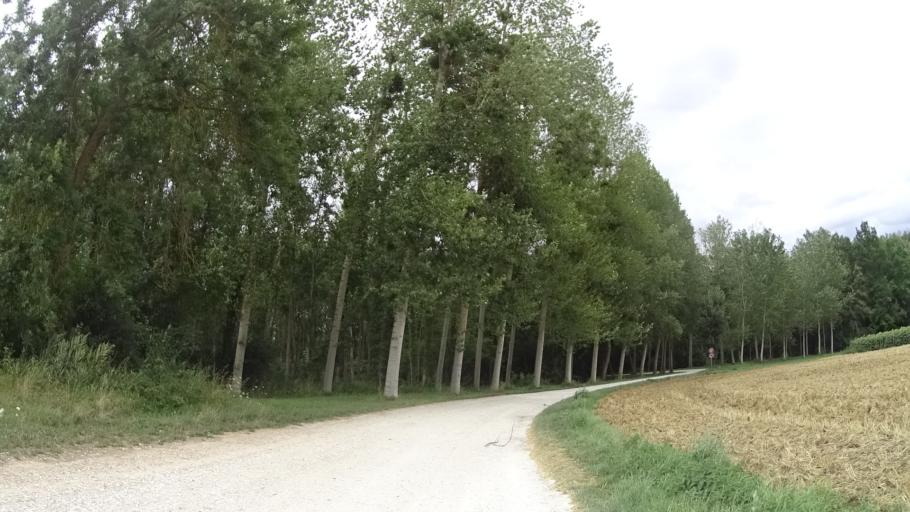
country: FR
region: Bourgogne
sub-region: Departement de l'Yonne
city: Joigny
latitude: 47.9545
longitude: 3.4141
